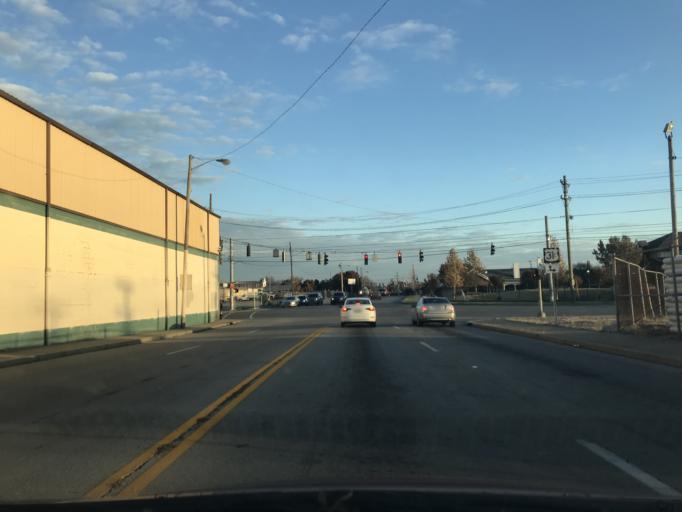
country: US
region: Kentucky
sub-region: Jefferson County
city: Louisville
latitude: 38.2507
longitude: -85.7330
